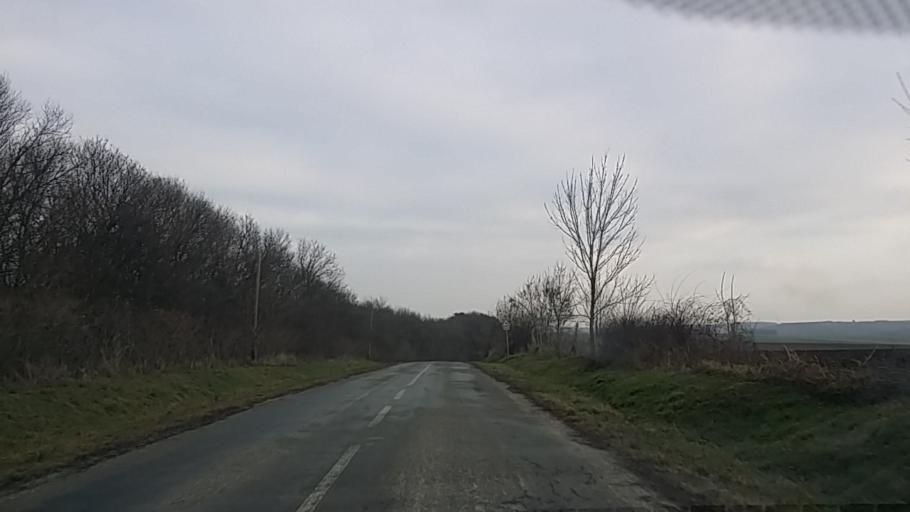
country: HU
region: Baranya
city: Lanycsok
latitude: 46.1002
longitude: 18.5467
